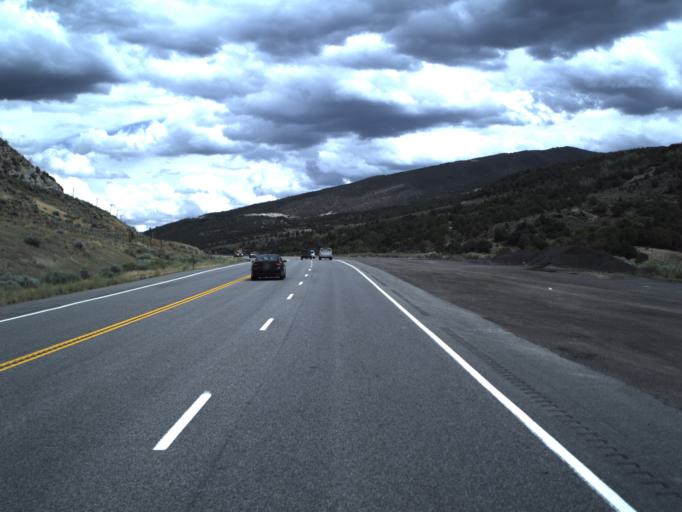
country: US
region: Utah
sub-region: Sanpete County
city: Fairview
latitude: 39.9290
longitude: -111.1886
